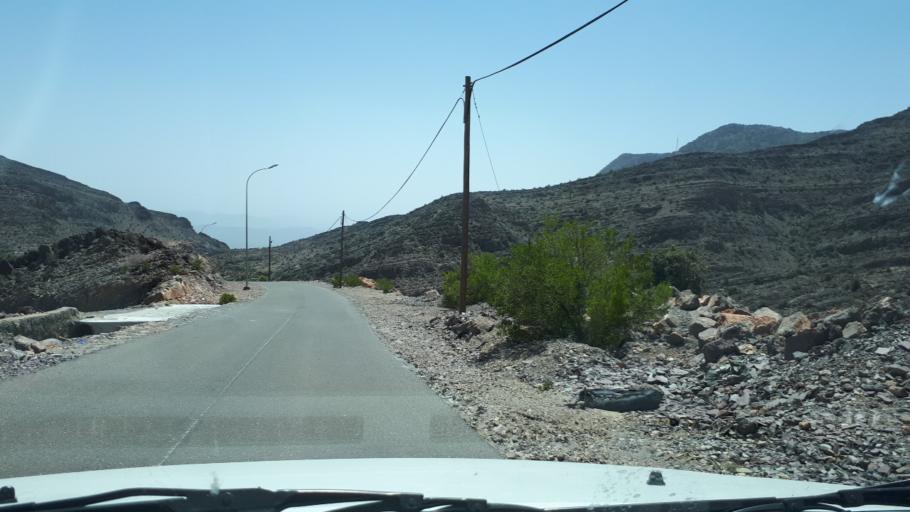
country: OM
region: Muhafazat ad Dakhiliyah
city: Izki
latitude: 23.0903
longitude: 57.7273
